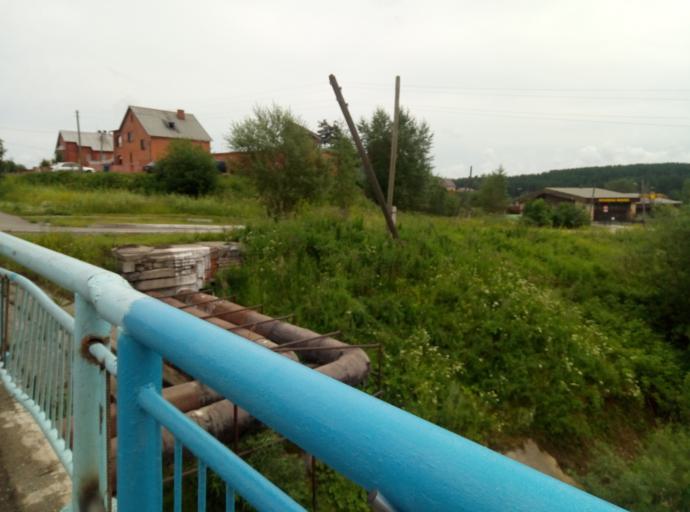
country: RU
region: Sverdlovsk
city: Krasnotur'insk
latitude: 59.7592
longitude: 60.1775
